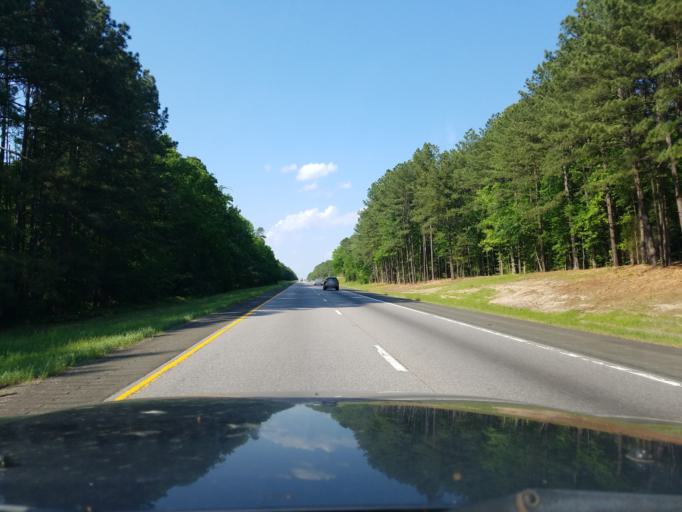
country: US
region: North Carolina
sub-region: Granville County
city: Butner
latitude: 36.0962
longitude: -78.7582
